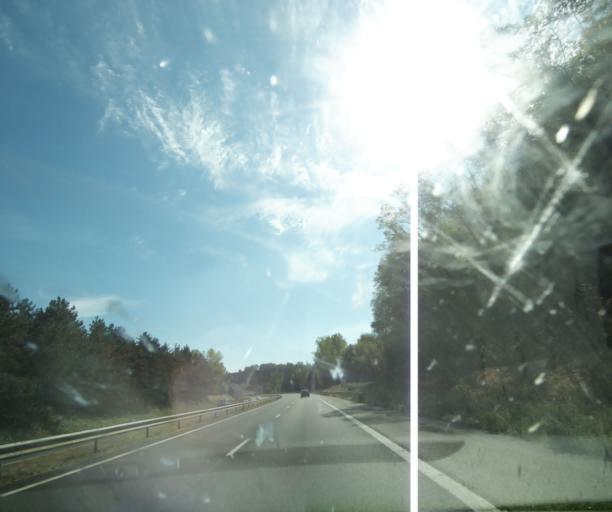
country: FR
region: Limousin
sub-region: Departement de la Correze
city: Brive-la-Gaillarde
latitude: 45.1323
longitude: 1.4918
